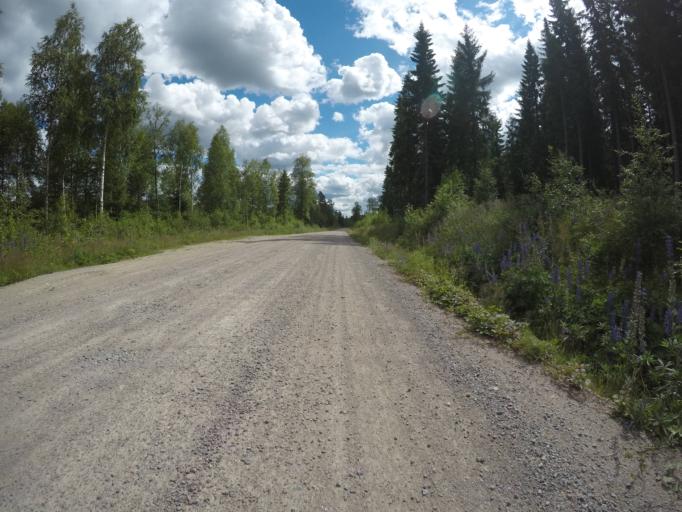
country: SE
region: Vaermland
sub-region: Filipstads Kommun
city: Lesjofors
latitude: 60.1282
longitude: 14.4253
